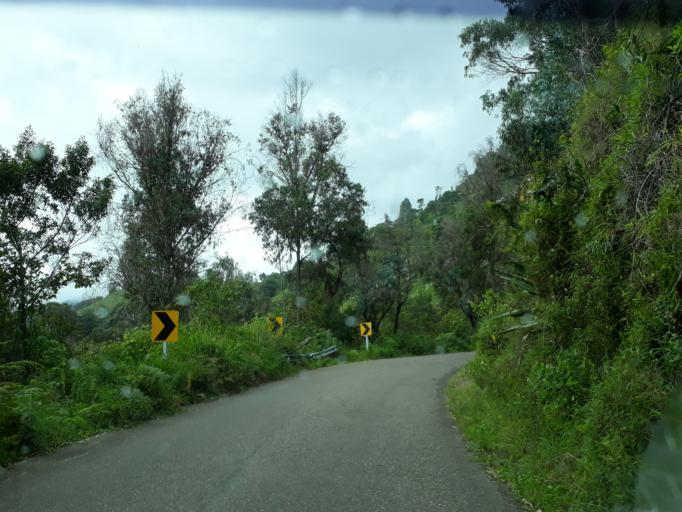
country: CO
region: Cundinamarca
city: Cabrera
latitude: 4.0205
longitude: -74.5115
